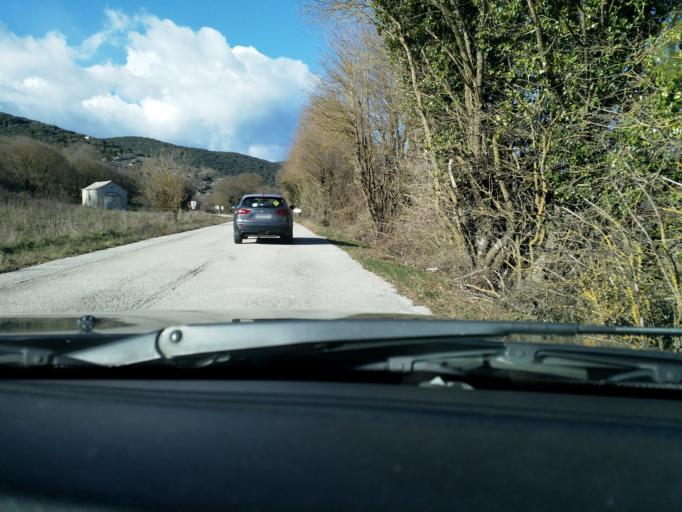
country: GR
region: Epirus
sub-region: Nomos Ioanninon
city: Kalpaki
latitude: 39.8775
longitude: 20.6822
